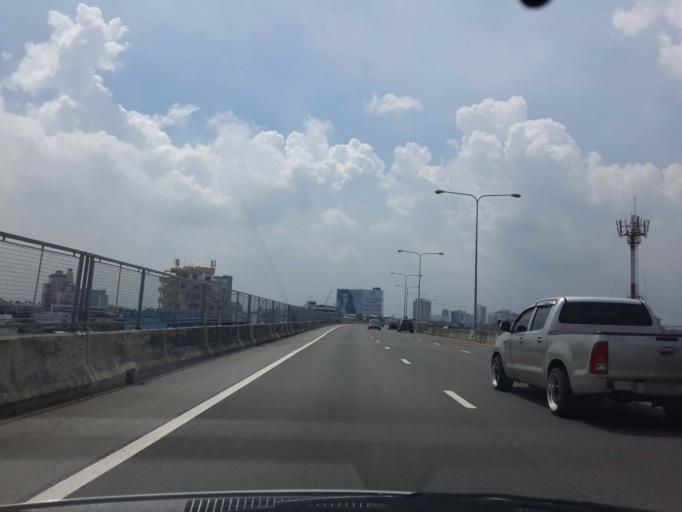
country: TH
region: Bangkok
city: Phra Khanong
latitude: 13.6934
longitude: 100.5988
